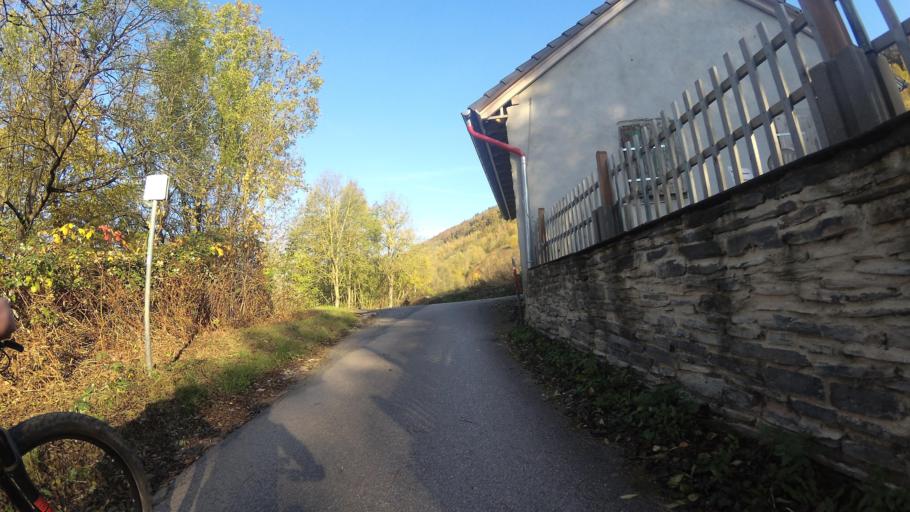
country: DE
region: Rheinland-Pfalz
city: Kenn
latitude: 49.7758
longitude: 6.6949
